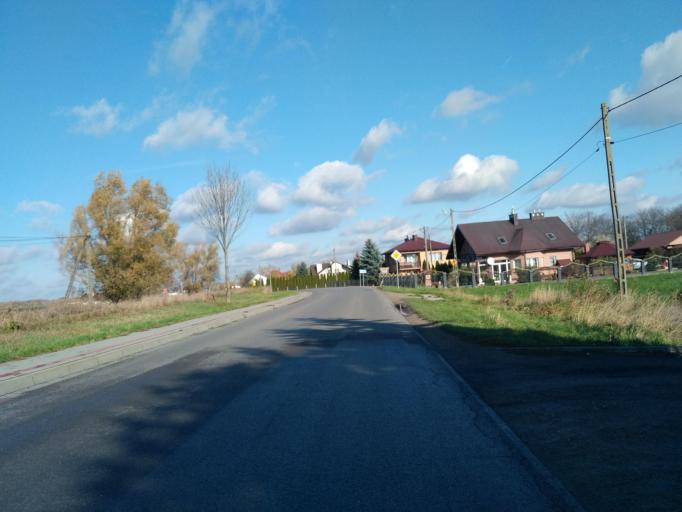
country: PL
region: Subcarpathian Voivodeship
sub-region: Powiat rzeszowski
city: Trzciana
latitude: 50.0830
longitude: 21.8402
